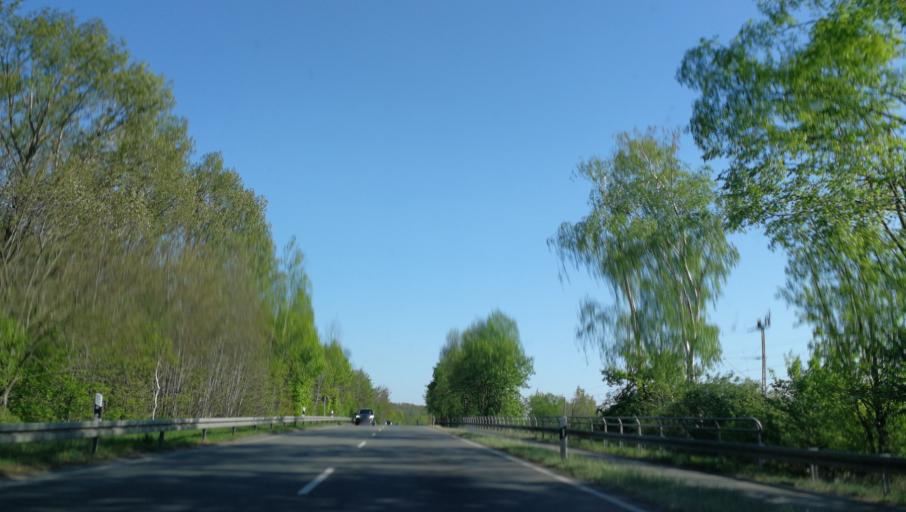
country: DE
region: North Rhine-Westphalia
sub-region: Regierungsbezirk Munster
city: Rheine
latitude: 52.2640
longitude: 7.4486
